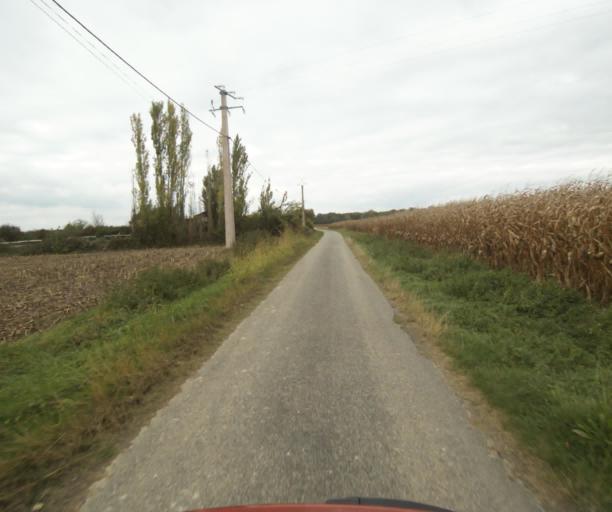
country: FR
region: Midi-Pyrenees
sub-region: Departement du Tarn-et-Garonne
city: Finhan
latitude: 43.8940
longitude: 1.2632
